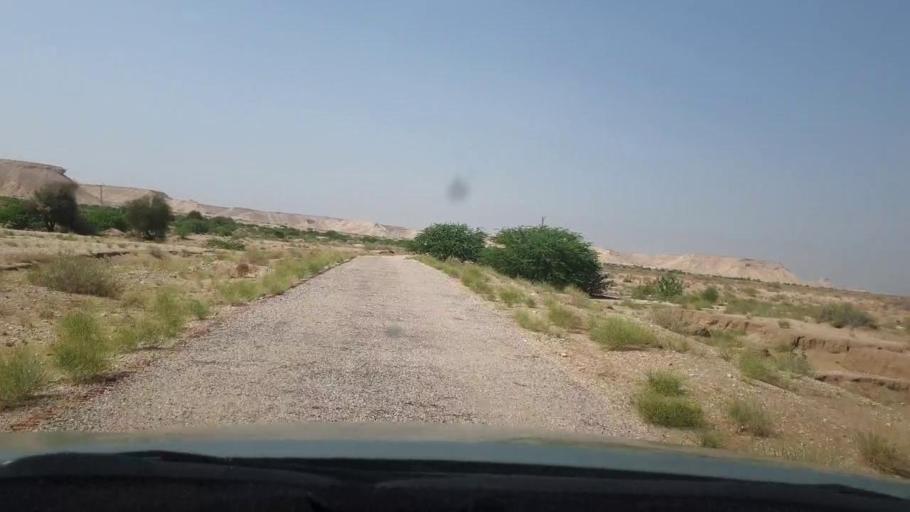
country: PK
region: Sindh
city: Kot Diji
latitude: 27.3303
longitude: 68.8159
